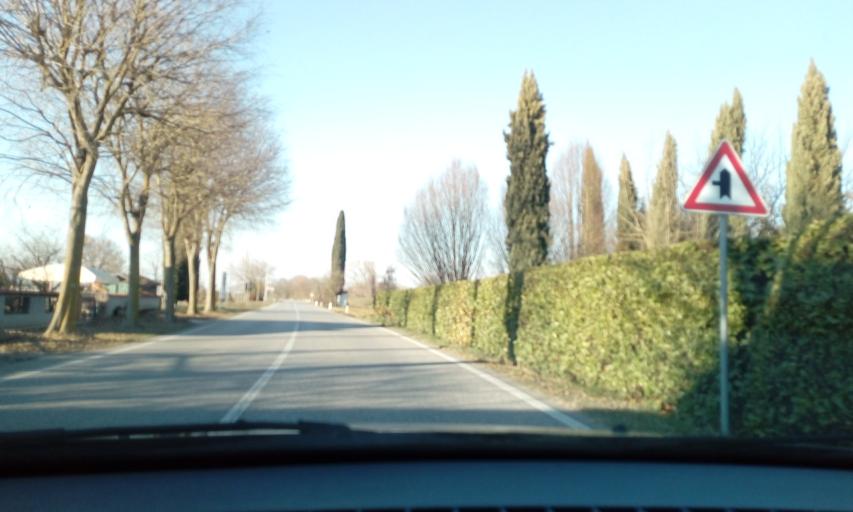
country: IT
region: Friuli Venezia Giulia
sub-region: Provincia di Gorizia
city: Medea
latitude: 45.9008
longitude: 13.4182
